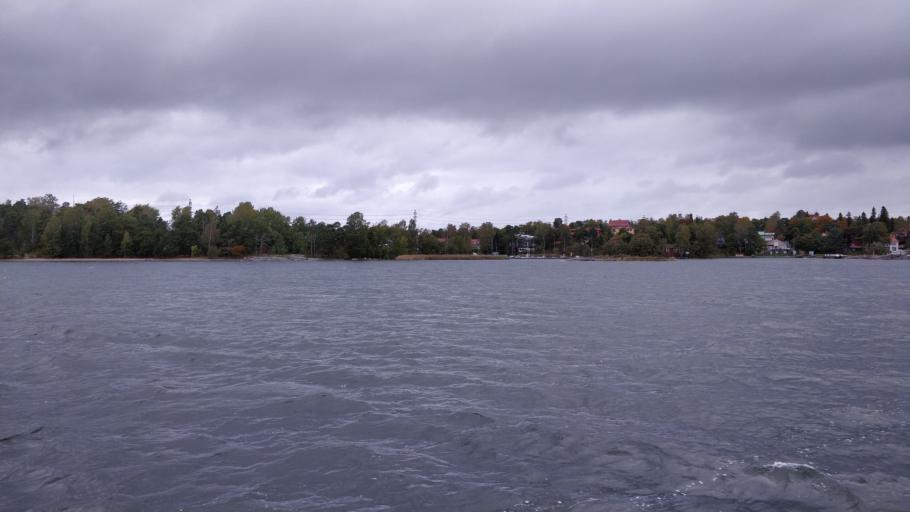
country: FI
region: Uusimaa
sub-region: Helsinki
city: Helsinki
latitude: 60.1780
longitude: 25.0014
